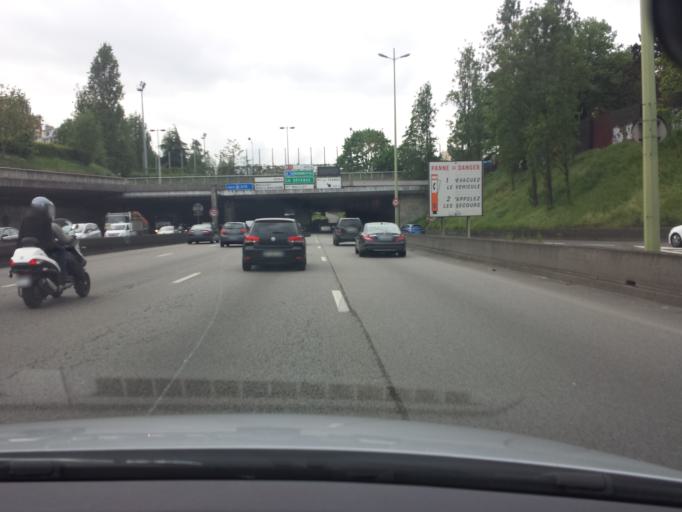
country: FR
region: Ile-de-France
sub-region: Departement des Hauts-de-Seine
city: Levallois-Perret
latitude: 48.8852
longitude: 2.2868
